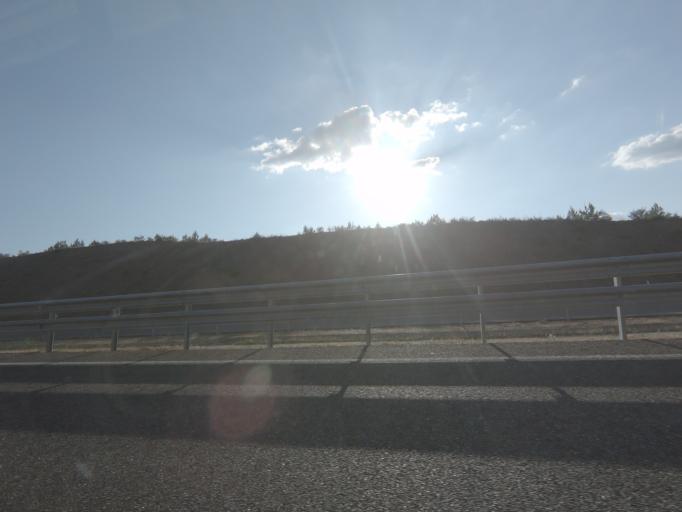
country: ES
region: Galicia
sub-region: Provincia de Ourense
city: Oimbra
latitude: 41.8734
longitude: -7.4326
